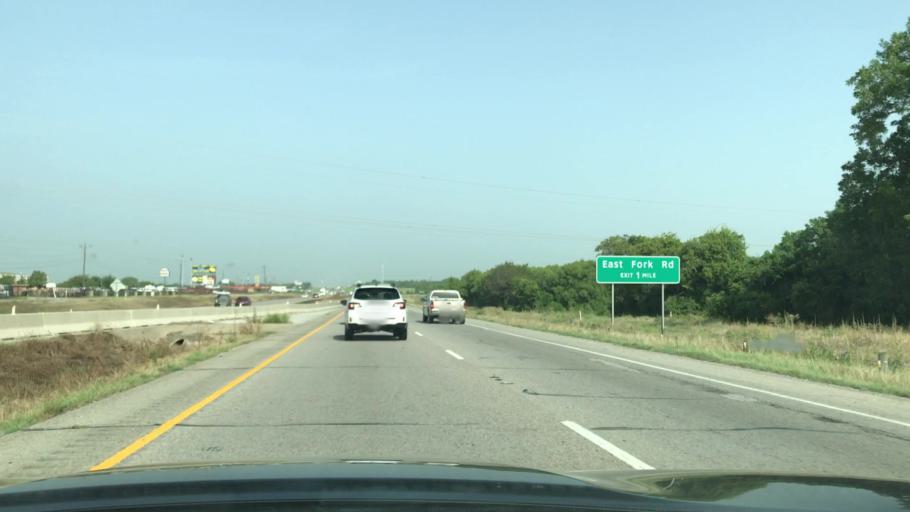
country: US
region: Texas
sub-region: Kaufman County
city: Forney
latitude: 32.7767
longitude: -96.5139
